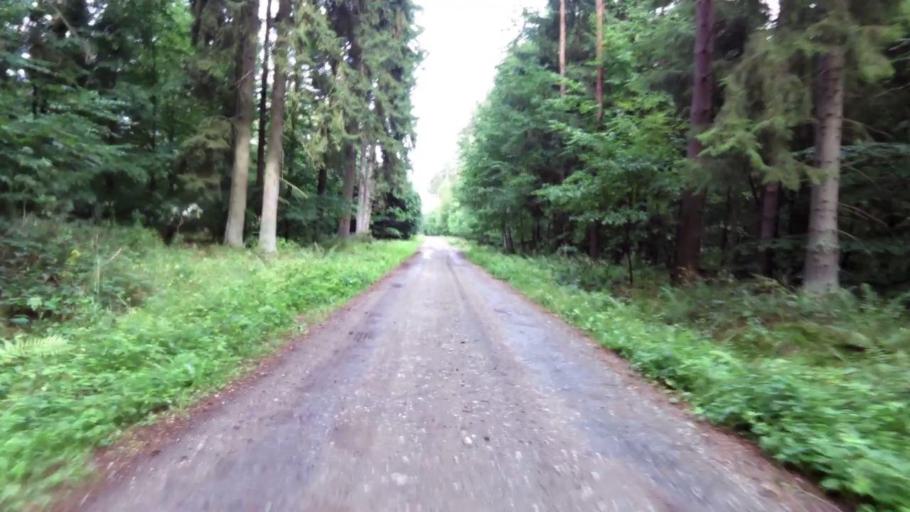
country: PL
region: West Pomeranian Voivodeship
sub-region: Powiat mysliborski
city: Debno
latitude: 52.8615
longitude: 14.6982
